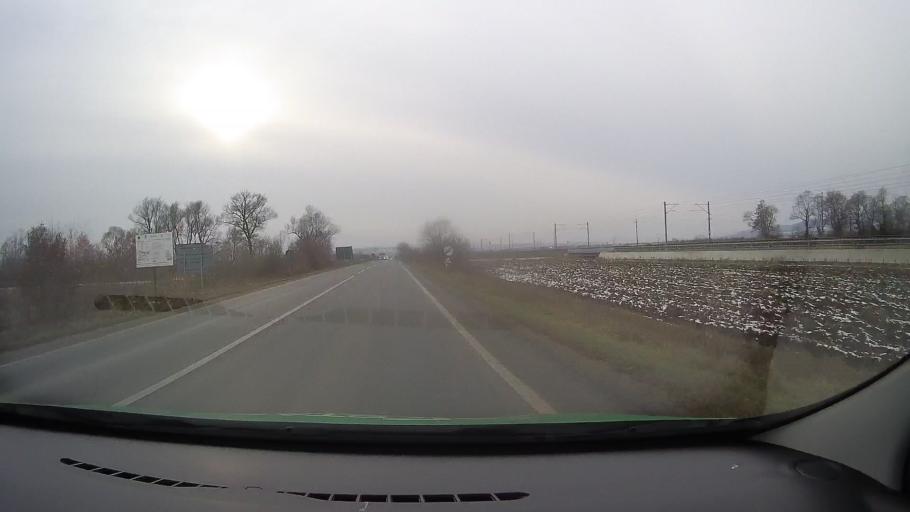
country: RO
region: Hunedoara
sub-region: Comuna Geoagiu
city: Geoagiu
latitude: 45.8816
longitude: 23.2458
